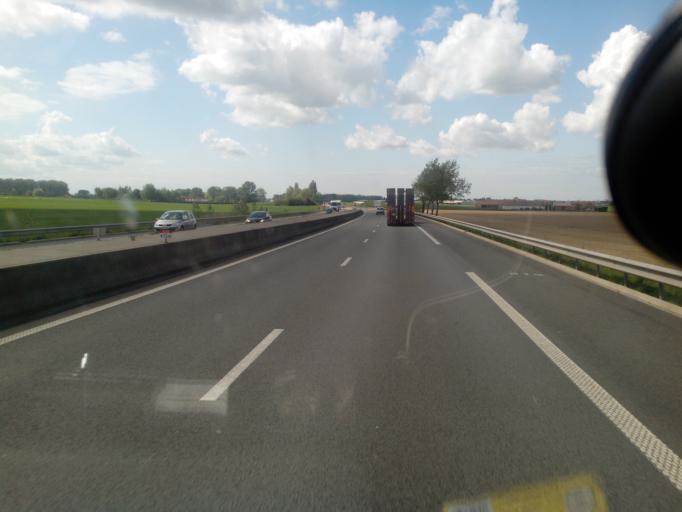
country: FR
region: Nord-Pas-de-Calais
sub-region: Departement du Nord
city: Quaedypre
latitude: 50.9411
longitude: 2.4560
